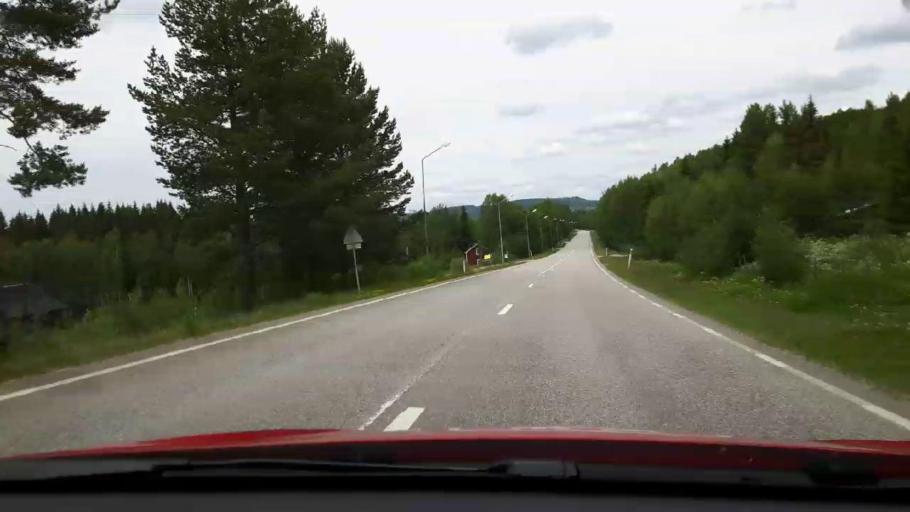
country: SE
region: Jaemtland
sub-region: Harjedalens Kommun
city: Sveg
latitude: 62.0669
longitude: 14.2730
